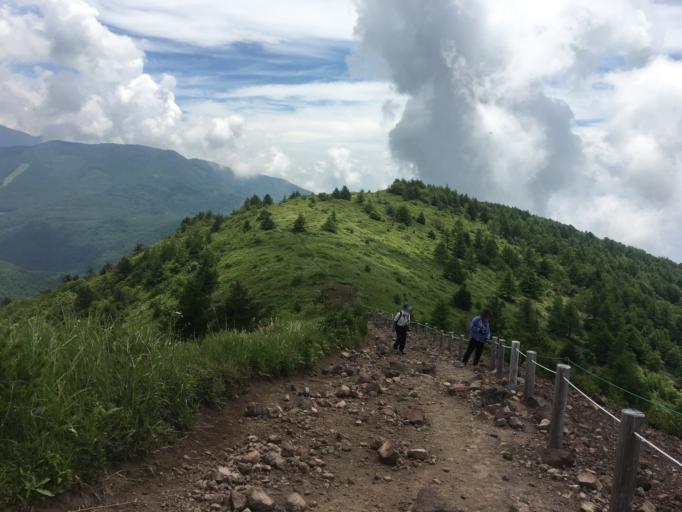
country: JP
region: Nagano
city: Ueda
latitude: 36.4284
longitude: 138.3896
